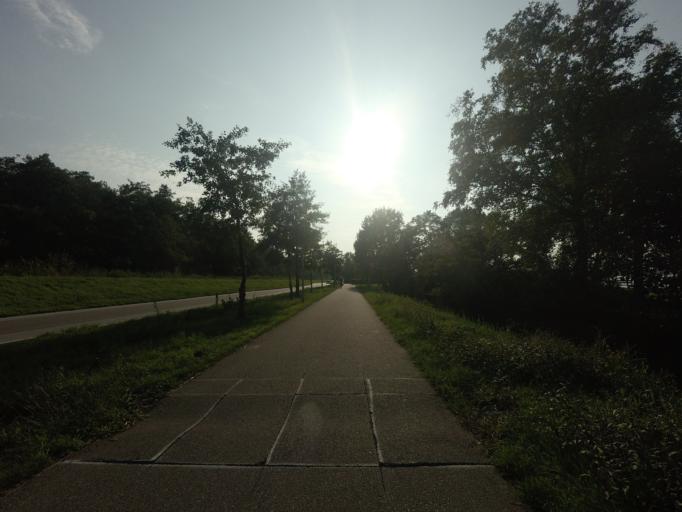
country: NL
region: Groningen
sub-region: Gemeente Haren
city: Haren
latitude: 53.1627
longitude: 6.5780
